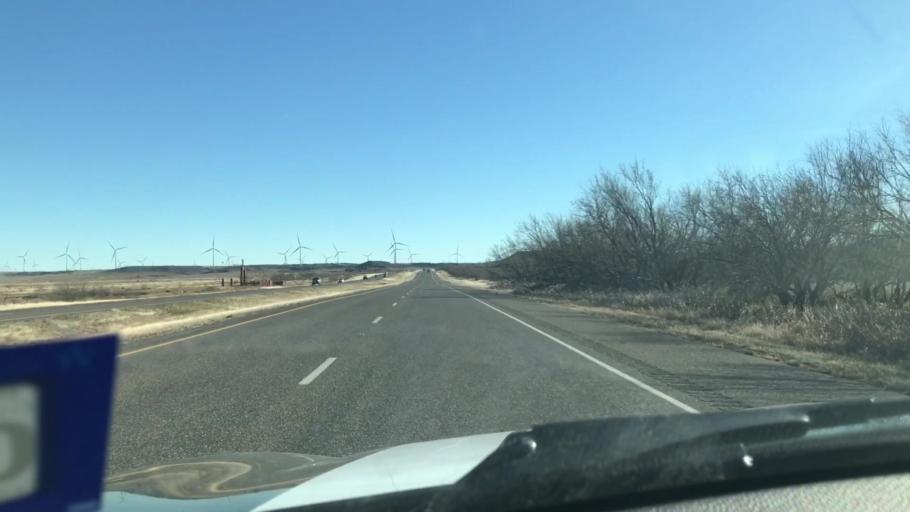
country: US
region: Texas
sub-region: Scurry County
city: Snyder
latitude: 32.9302
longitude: -101.0690
